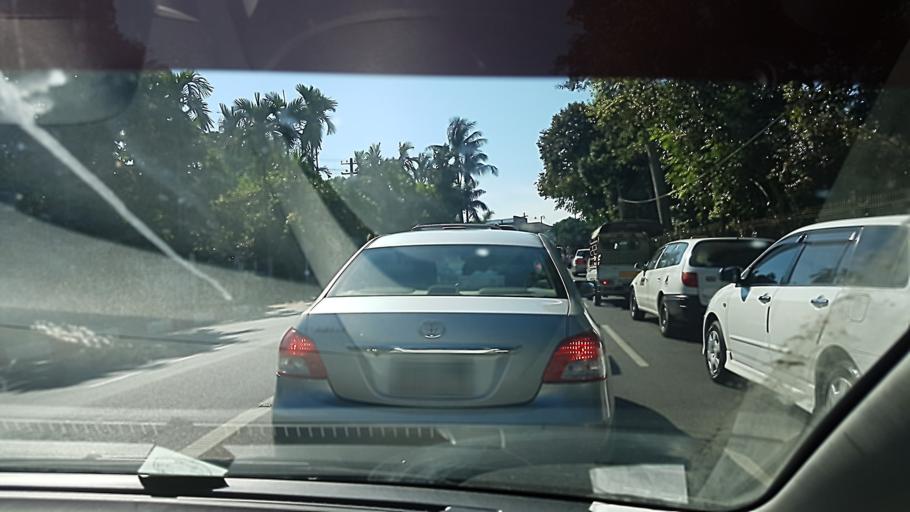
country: MM
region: Yangon
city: Yangon
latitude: 16.8289
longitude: 96.1395
